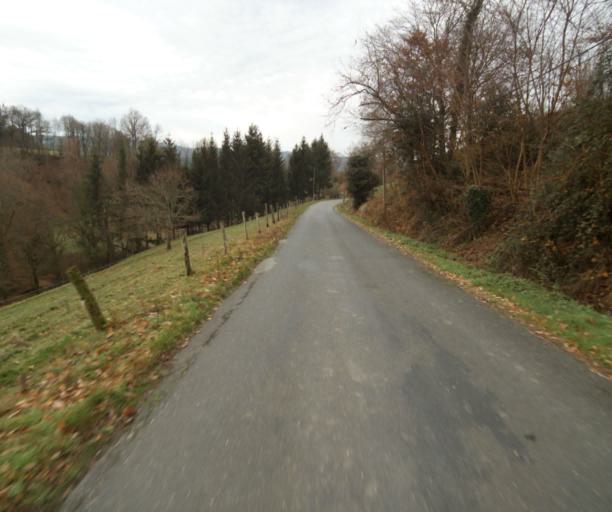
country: FR
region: Limousin
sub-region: Departement de la Correze
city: Tulle
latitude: 45.2484
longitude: 1.7359
